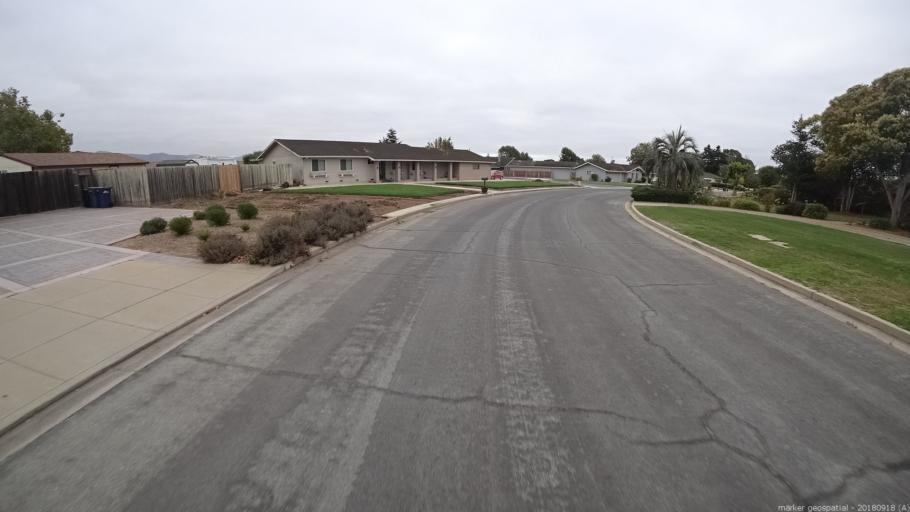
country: US
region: California
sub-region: Monterey County
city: Prunedale
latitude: 36.7479
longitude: -121.6279
